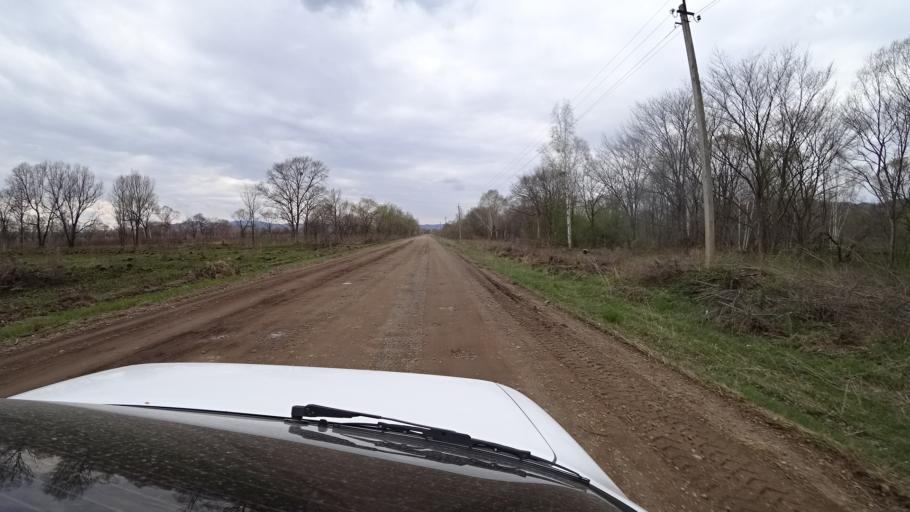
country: RU
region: Primorskiy
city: Novopokrovka
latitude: 45.5597
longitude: 134.3455
